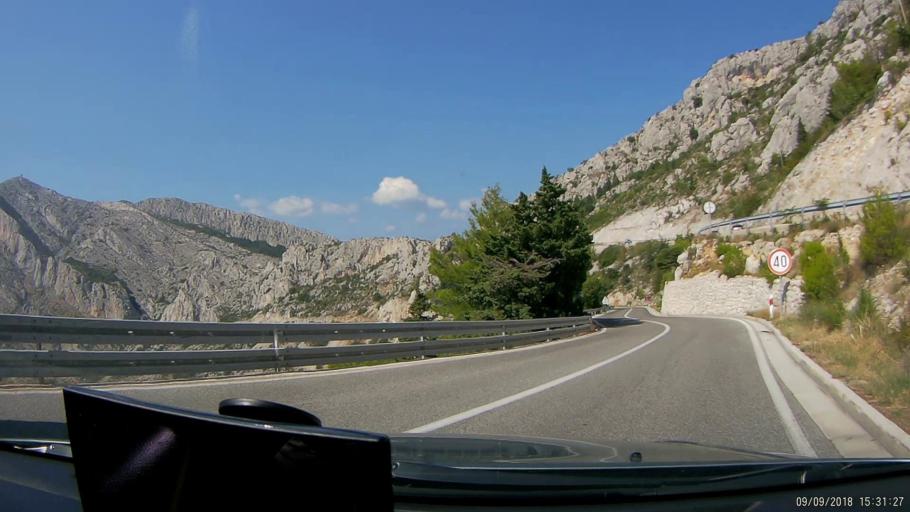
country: HR
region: Splitsko-Dalmatinska
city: Donja Brela
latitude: 43.3985
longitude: 16.8917
